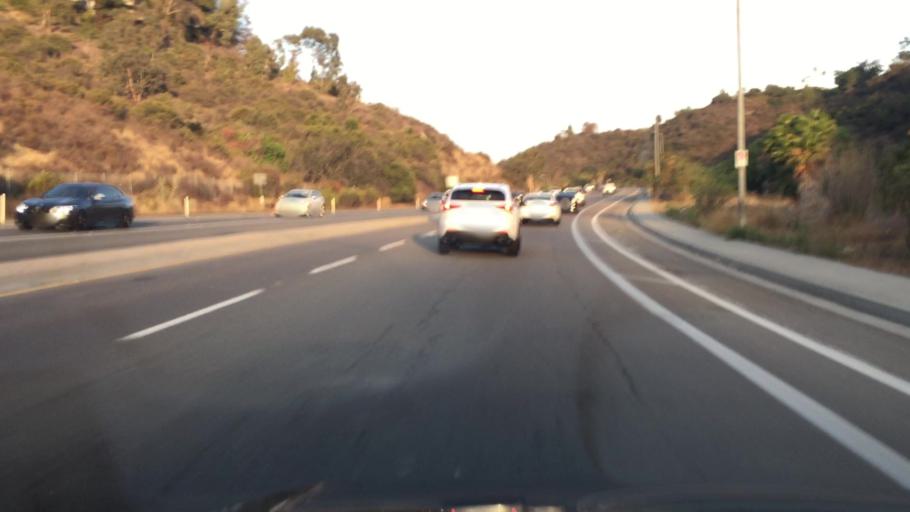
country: US
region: California
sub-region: San Diego County
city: Lemon Grove
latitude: 32.7715
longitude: -117.0941
